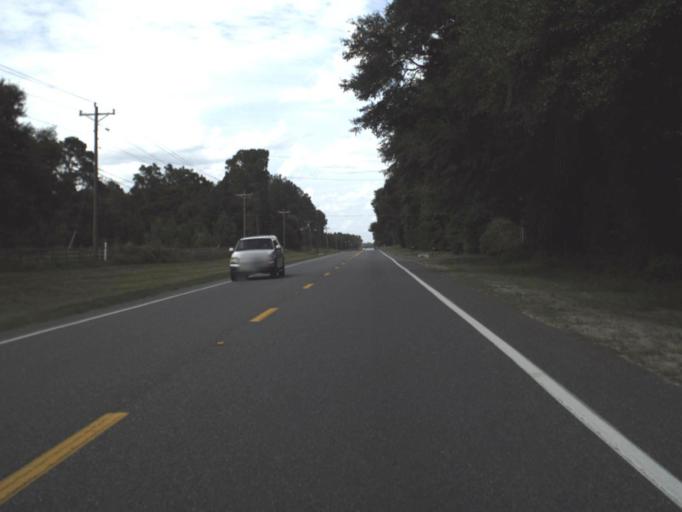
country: US
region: Florida
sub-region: Columbia County
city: Lake City
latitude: 30.0850
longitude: -82.6901
